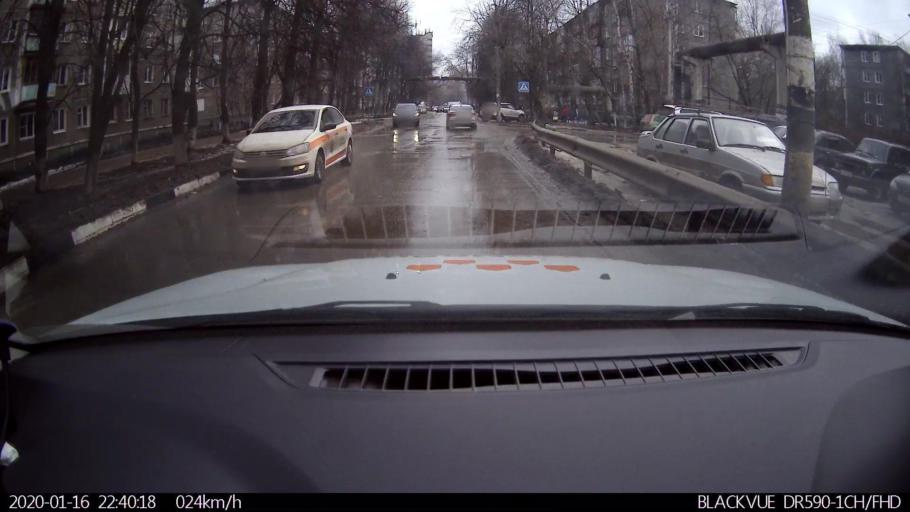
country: RU
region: Nizjnij Novgorod
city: Nizhniy Novgorod
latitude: 56.2773
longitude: 43.9177
